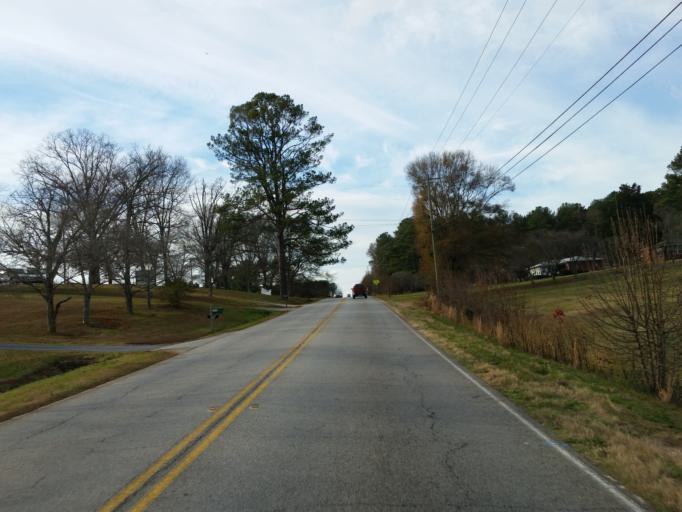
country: US
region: Georgia
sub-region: Paulding County
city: Hiram
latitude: 33.9119
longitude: -84.7613
